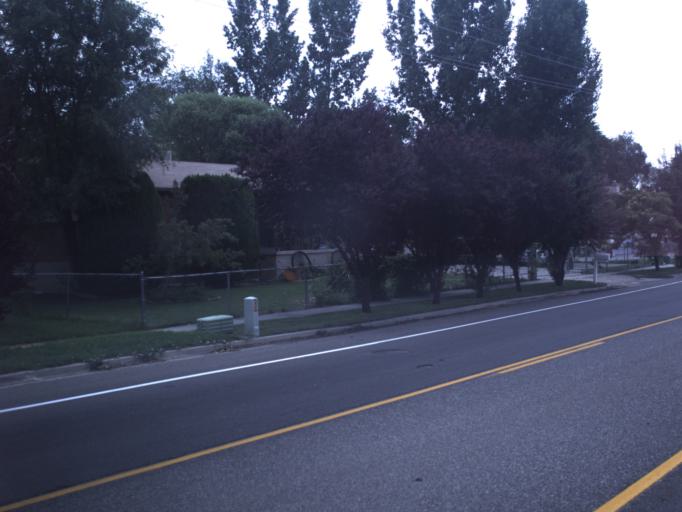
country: US
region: Utah
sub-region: Davis County
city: Clinton
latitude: 41.1643
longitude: -112.0645
